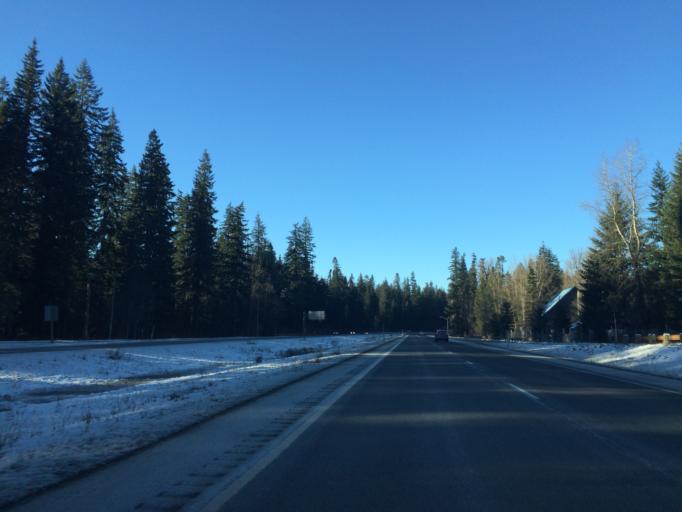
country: US
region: Washington
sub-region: Kittitas County
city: Cle Elum
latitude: 47.3066
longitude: -121.3079
